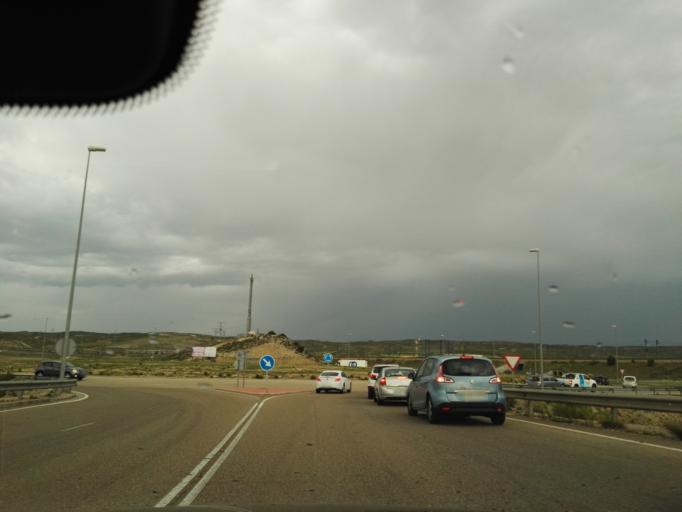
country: ES
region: Aragon
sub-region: Provincia de Zaragoza
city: Montecanal
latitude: 41.6288
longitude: -0.9902
